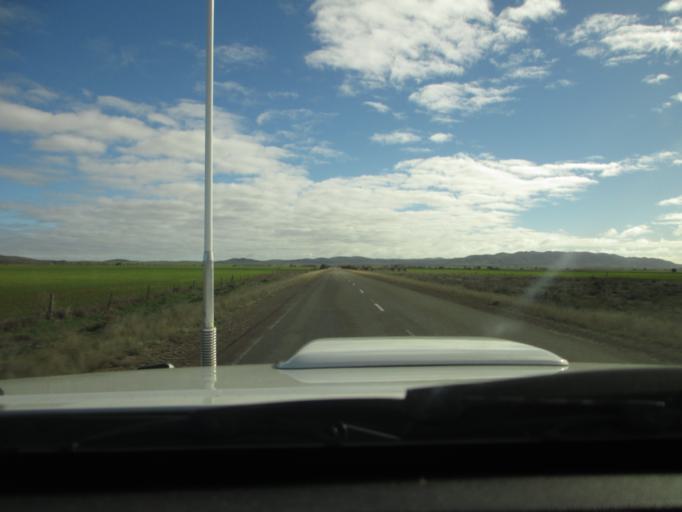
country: AU
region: South Australia
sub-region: Peterborough
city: Peterborough
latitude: -32.6589
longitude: 138.6045
